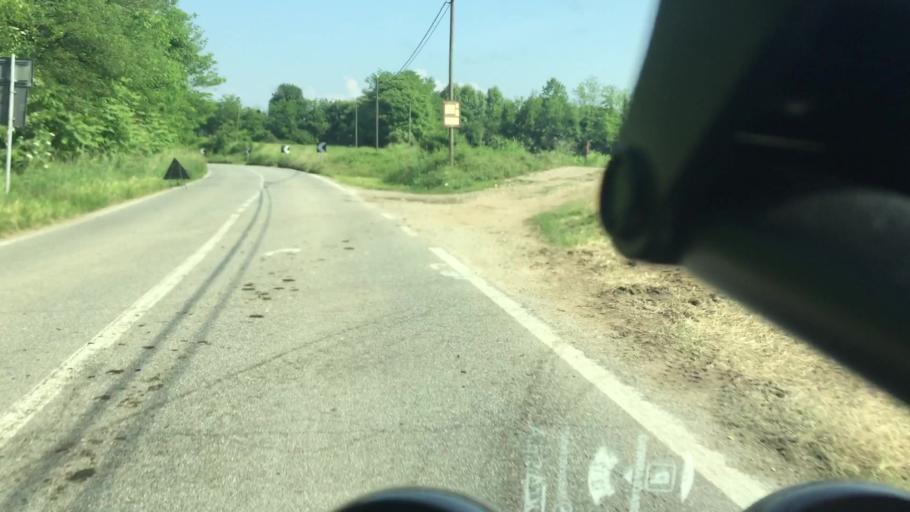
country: IT
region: Lombardy
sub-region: Provincia di Bergamo
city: Pontirolo Nuovo
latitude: 45.5534
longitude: 9.5664
